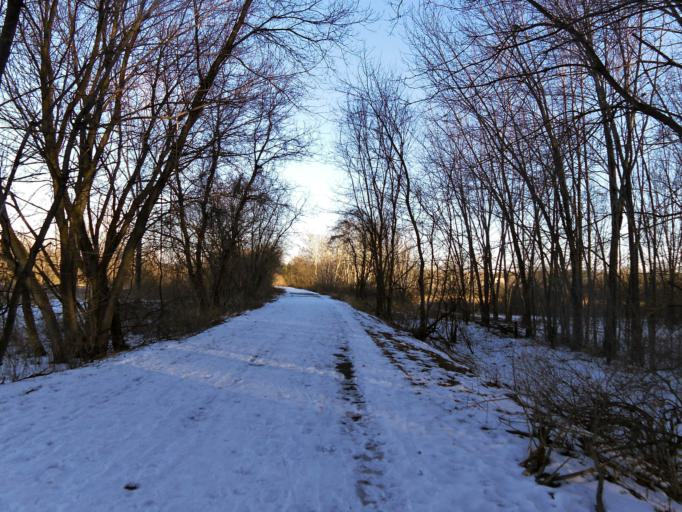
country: US
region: Minnesota
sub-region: Washington County
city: Stillwater
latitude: 45.0704
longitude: -92.8486
